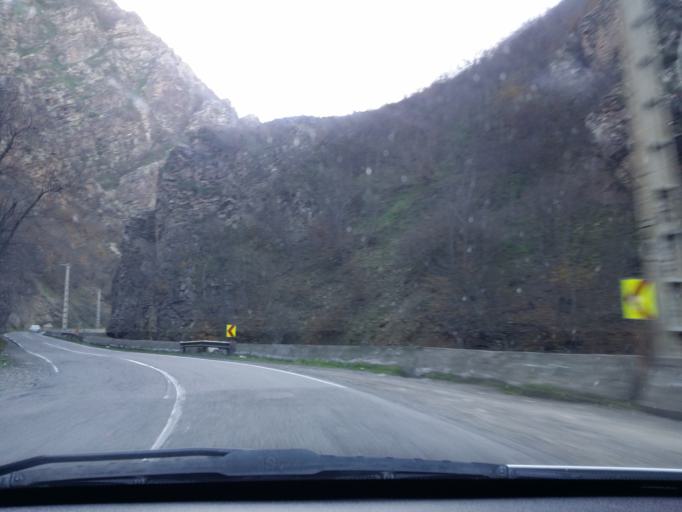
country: IR
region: Mazandaran
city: Chalus
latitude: 36.2877
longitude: 51.2421
